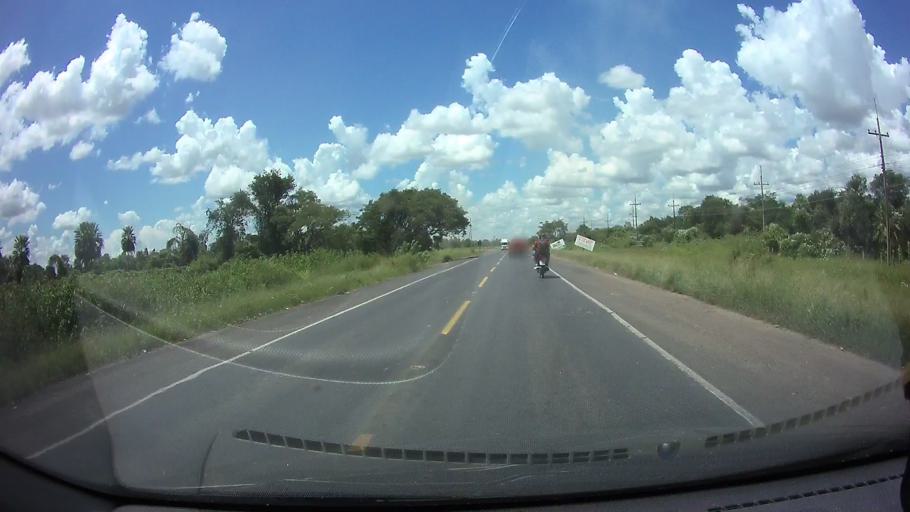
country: PY
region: Central
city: Colonia Mariano Roque Alonso
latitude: -25.1773
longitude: -57.5819
